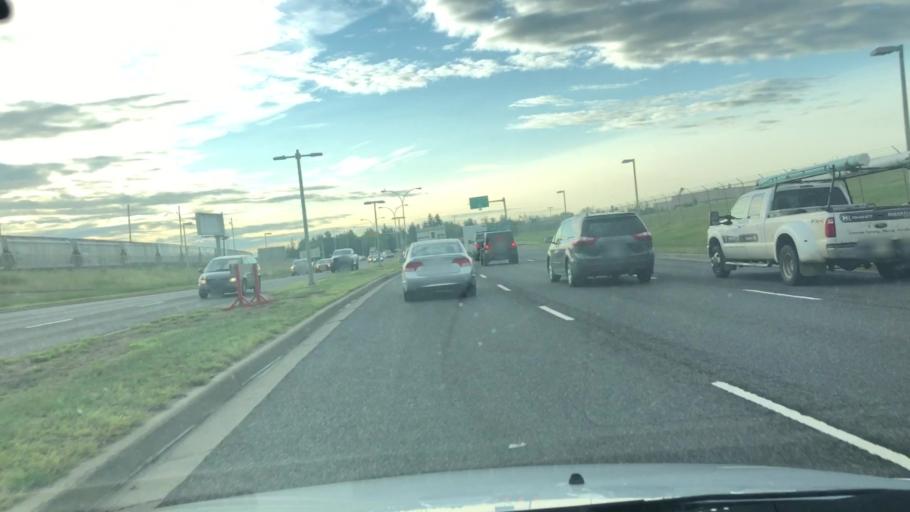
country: CA
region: Alberta
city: Edmonton
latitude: 53.5817
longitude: -113.5113
